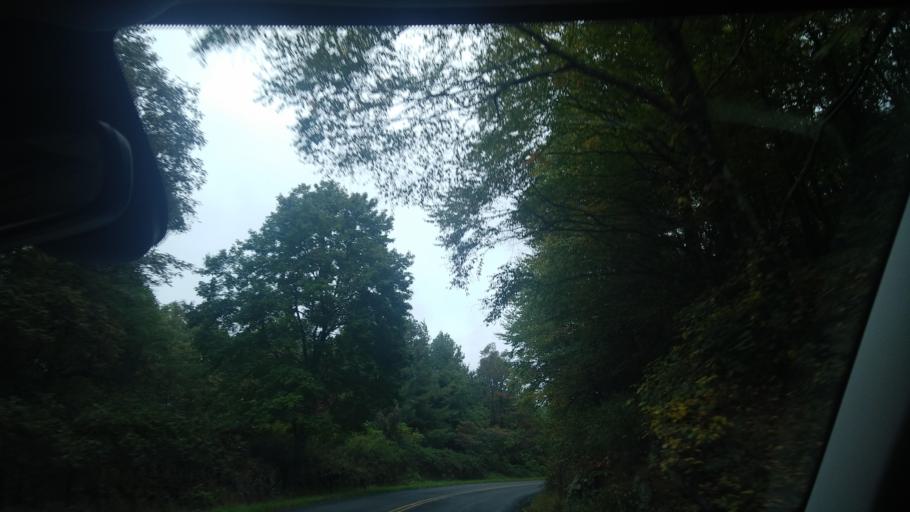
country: US
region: Virginia
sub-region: Carroll County
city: Cana
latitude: 36.6714
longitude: -80.6439
